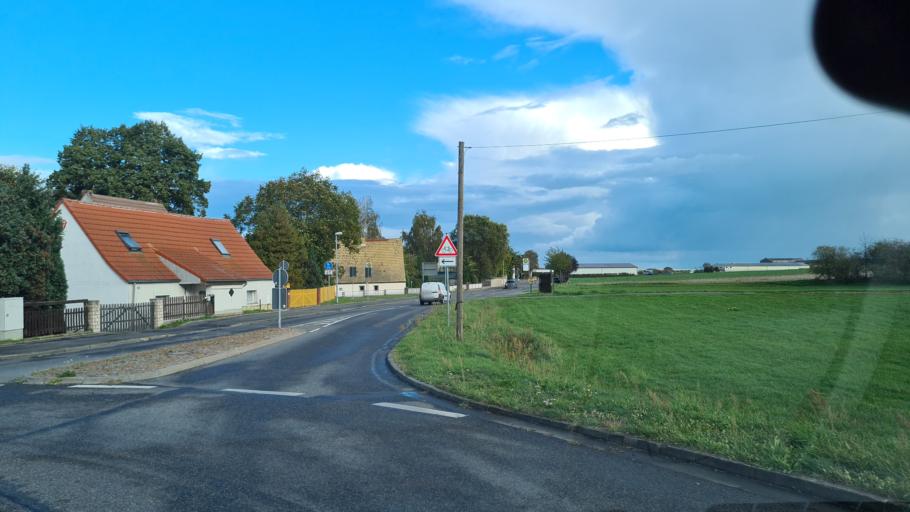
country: DE
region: Saxony
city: Dahlen
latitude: 51.3611
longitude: 13.0380
